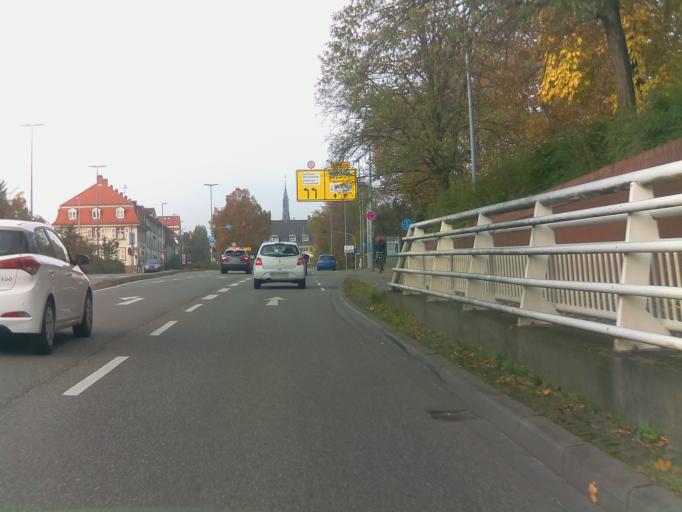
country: DE
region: Baden-Wuerttemberg
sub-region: Karlsruhe Region
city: Heidelberg
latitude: 49.3960
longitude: 8.6856
